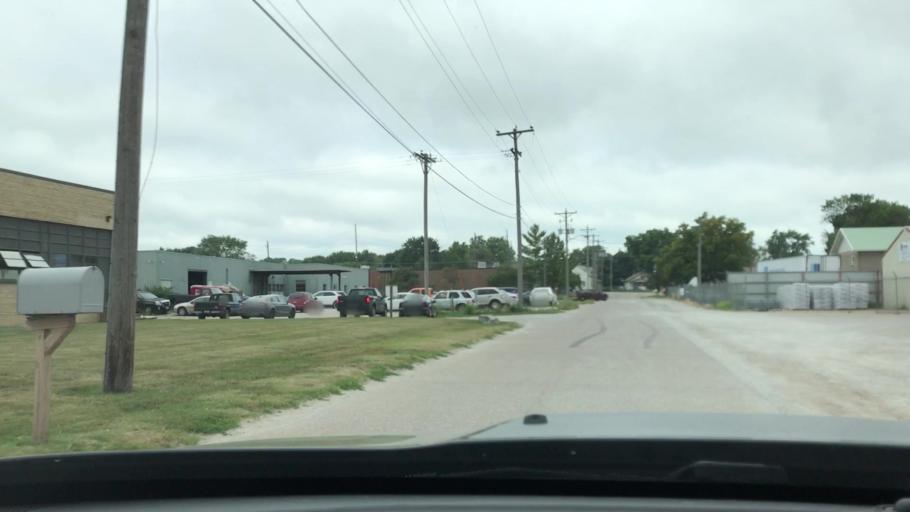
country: US
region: Illinois
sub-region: Rock Island County
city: Rock Island
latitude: 41.5098
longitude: -90.6166
